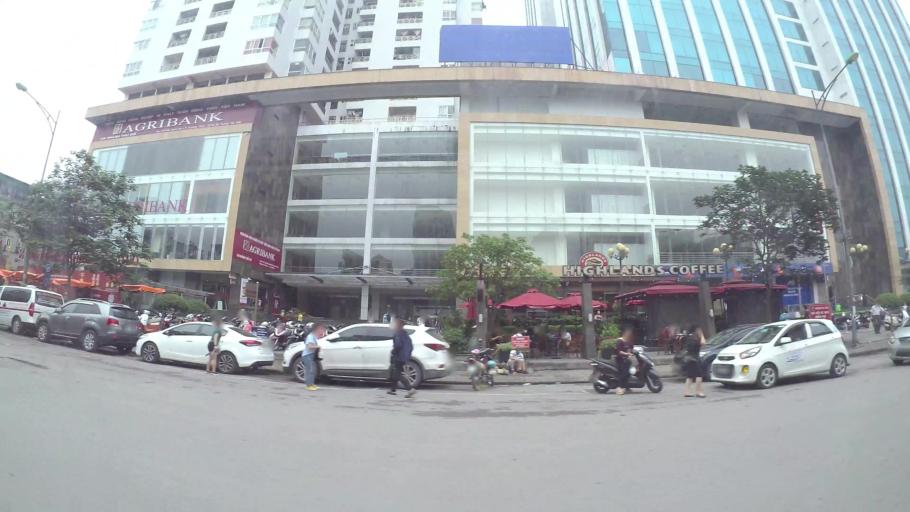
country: VN
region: Ha Noi
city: Hai BaTrung
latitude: 20.9971
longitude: 105.8501
